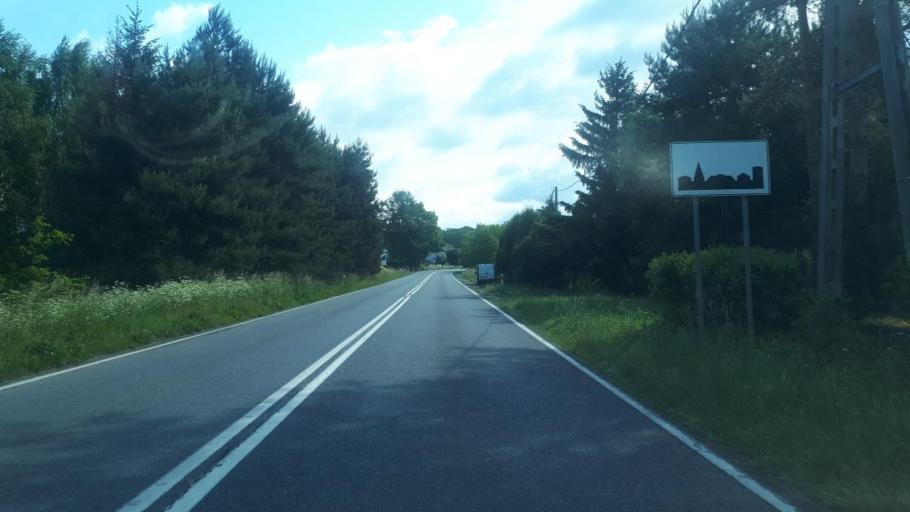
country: PL
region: Silesian Voivodeship
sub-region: Powiat pszczynski
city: Gora
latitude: 49.9745
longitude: 19.1196
